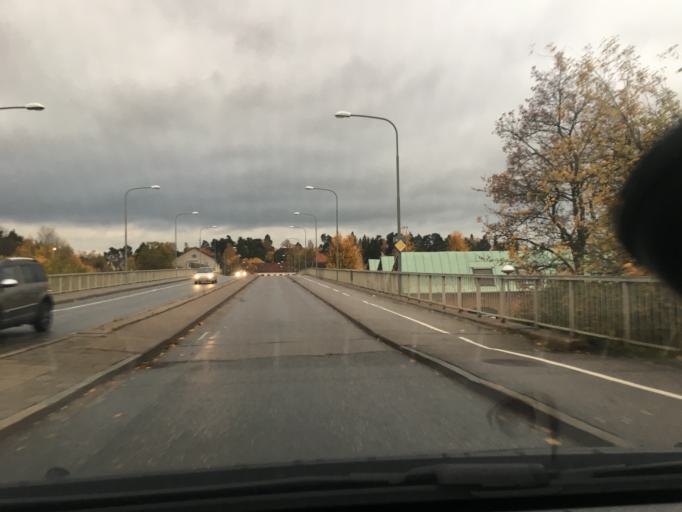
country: SE
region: Stockholm
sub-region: Stockholms Kommun
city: Kista
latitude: 59.3827
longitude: 17.9028
